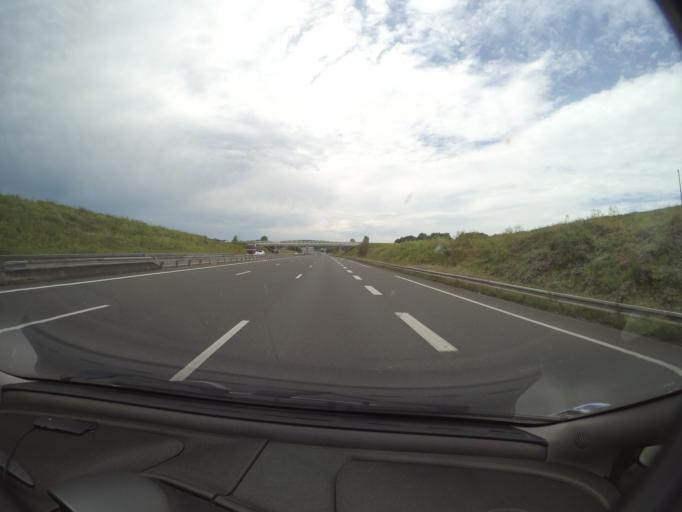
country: FR
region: Pays de la Loire
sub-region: Departement de la Sarthe
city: Neuville-sur-Sarthe
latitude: 48.0538
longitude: 0.1795
